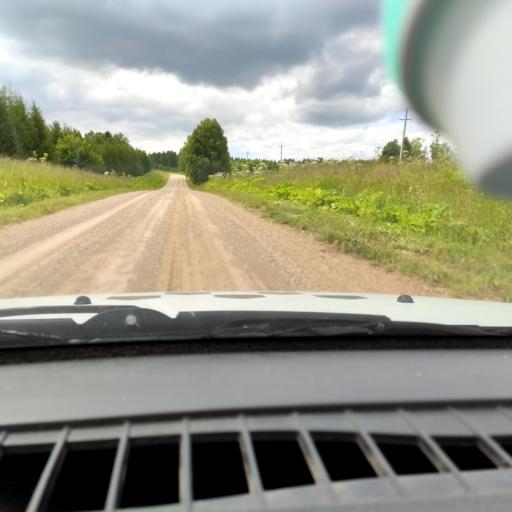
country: RU
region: Perm
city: Suksun
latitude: 57.2136
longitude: 57.6869
